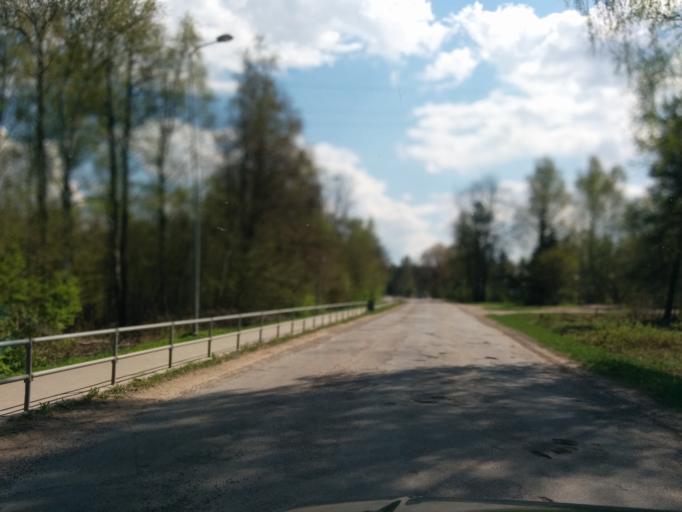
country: LV
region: Ozolnieku
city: Ozolnieki
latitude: 56.6135
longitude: 23.7844
